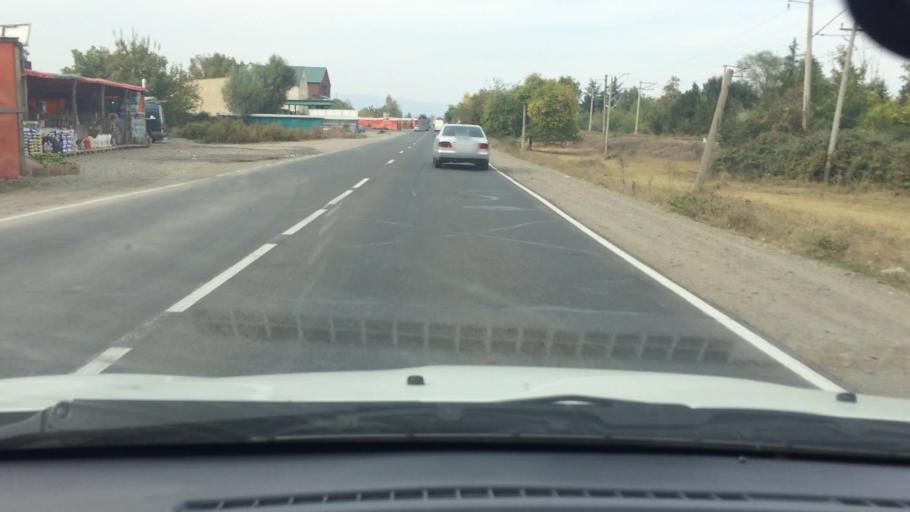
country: GE
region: Kvemo Kartli
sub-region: Marneuli
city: Marneuli
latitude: 41.4174
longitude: 44.8262
